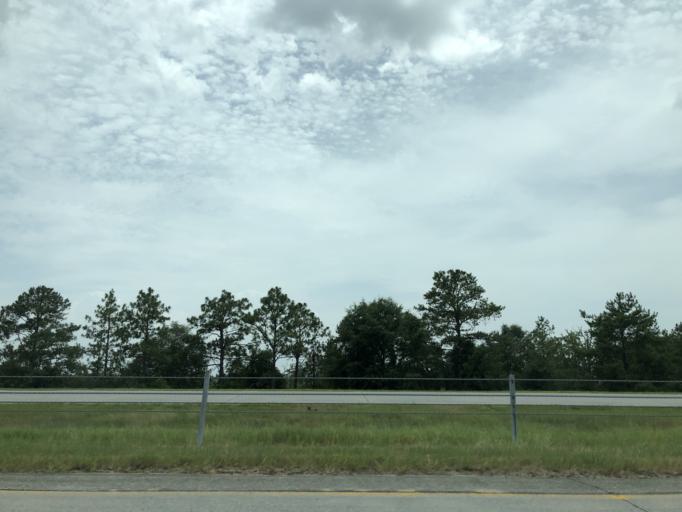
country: US
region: Georgia
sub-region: Toombs County
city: Lyons
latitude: 32.3910
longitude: -82.2896
